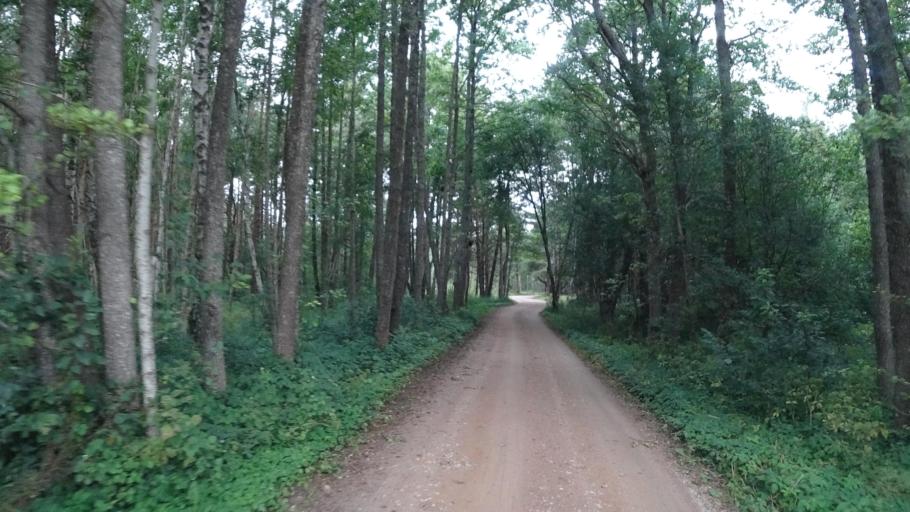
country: LV
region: Liepaja
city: Vec-Liepaja
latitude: 56.6240
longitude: 21.0443
